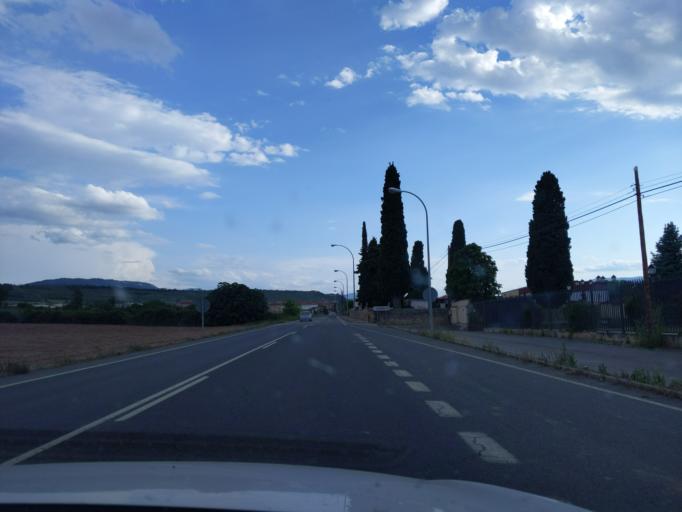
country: ES
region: La Rioja
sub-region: Provincia de La Rioja
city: Alberite
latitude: 42.4123
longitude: -2.4356
